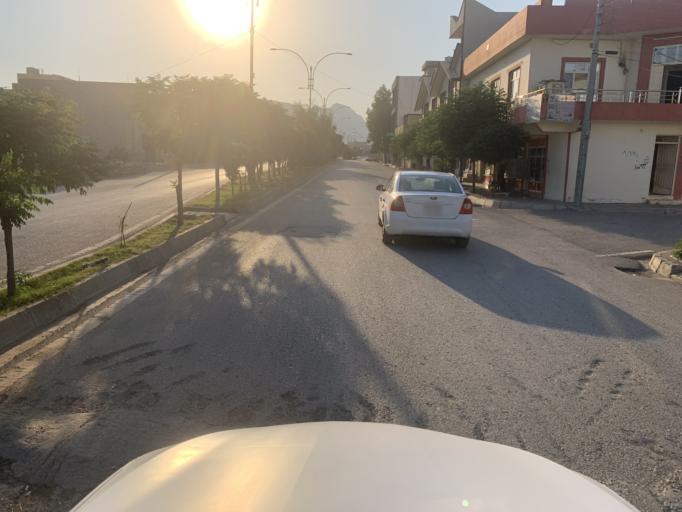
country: IQ
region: As Sulaymaniyah
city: Raniye
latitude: 36.2389
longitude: 44.8789
